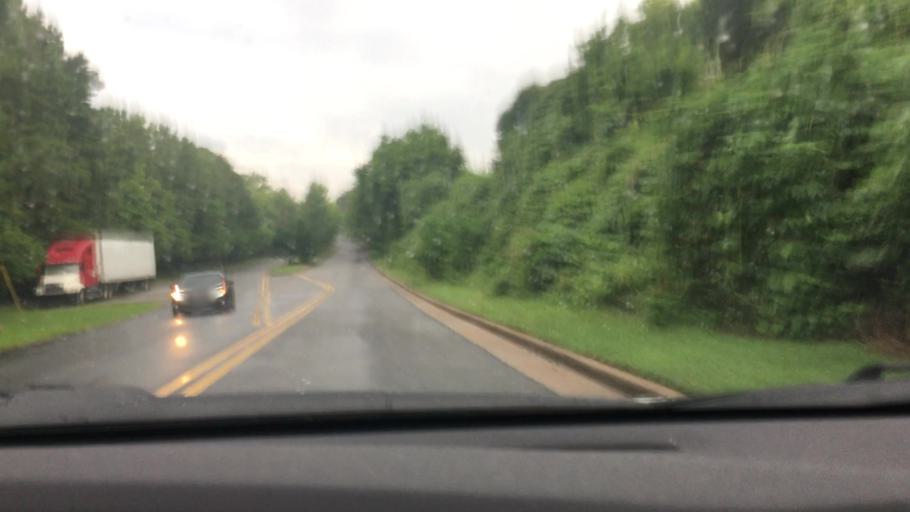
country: US
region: Georgia
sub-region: Fulton County
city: Union City
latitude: 33.6550
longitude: -84.5215
